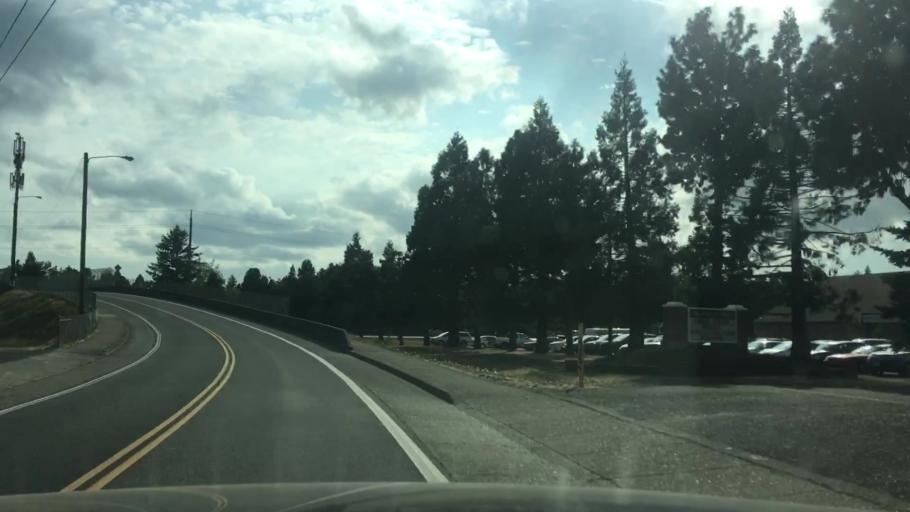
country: US
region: Oregon
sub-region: Lane County
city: Eugene
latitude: 44.0905
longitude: -123.0880
